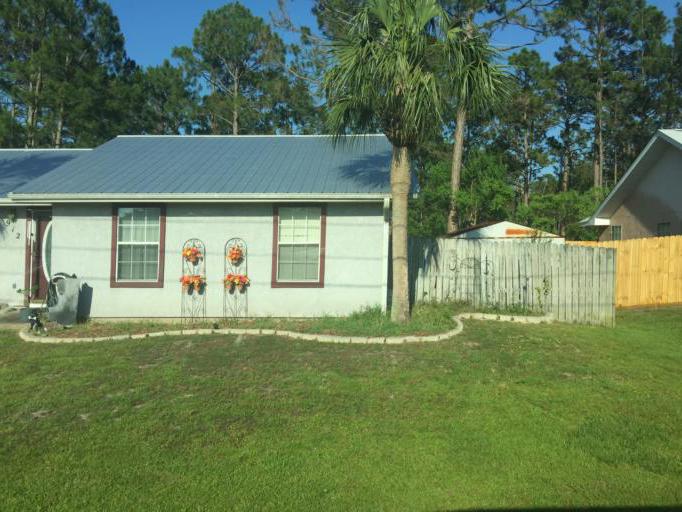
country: US
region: Florida
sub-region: Bay County
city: Panama City Beach
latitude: 30.2076
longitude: -85.8273
